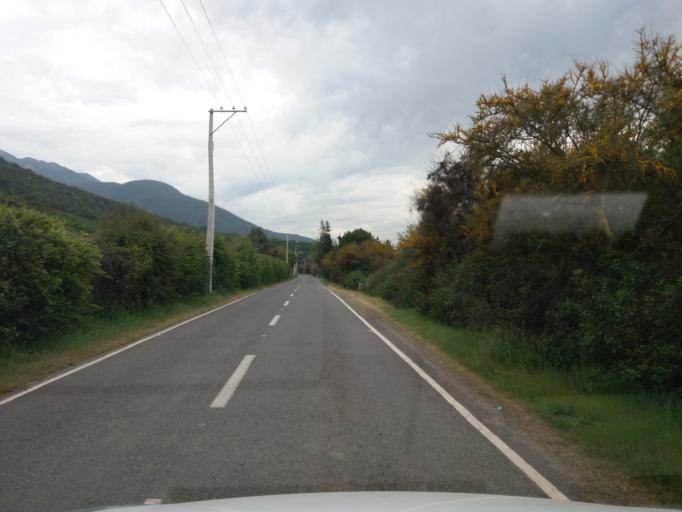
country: CL
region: Valparaiso
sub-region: Provincia de Quillota
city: Quillota
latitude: -32.9052
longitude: -71.1033
